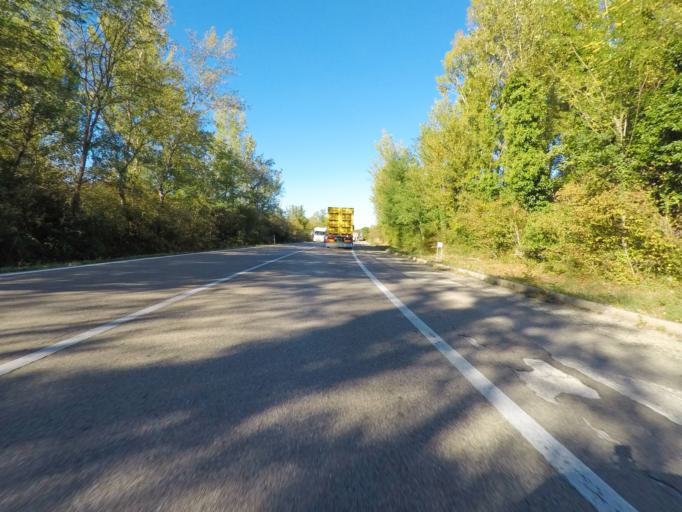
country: IT
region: Tuscany
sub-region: Provincia di Siena
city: Rosia
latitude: 43.2008
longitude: 11.2762
